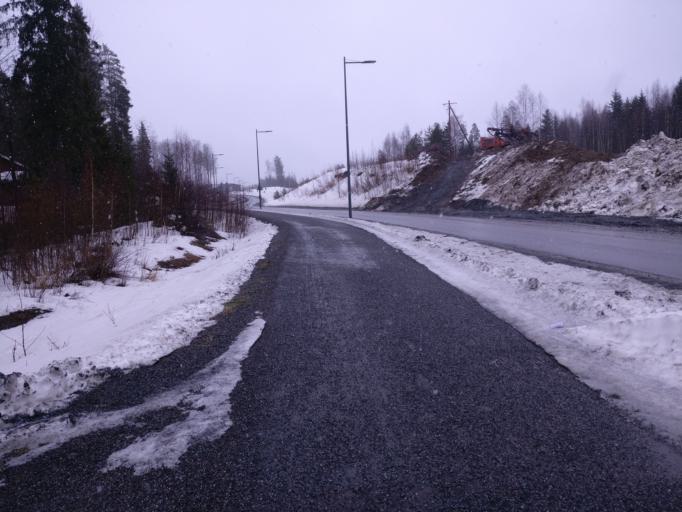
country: FI
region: Pirkanmaa
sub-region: Tampere
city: Tampere
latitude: 61.4302
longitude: 23.8203
